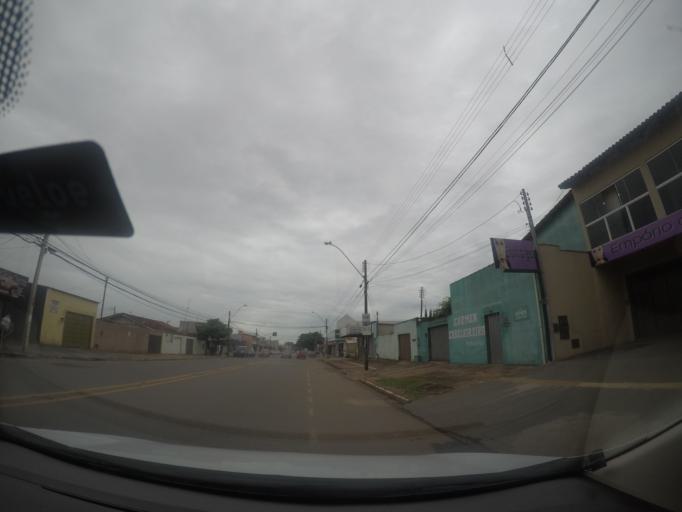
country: BR
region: Goias
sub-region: Goiania
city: Goiania
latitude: -16.6185
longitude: -49.2909
